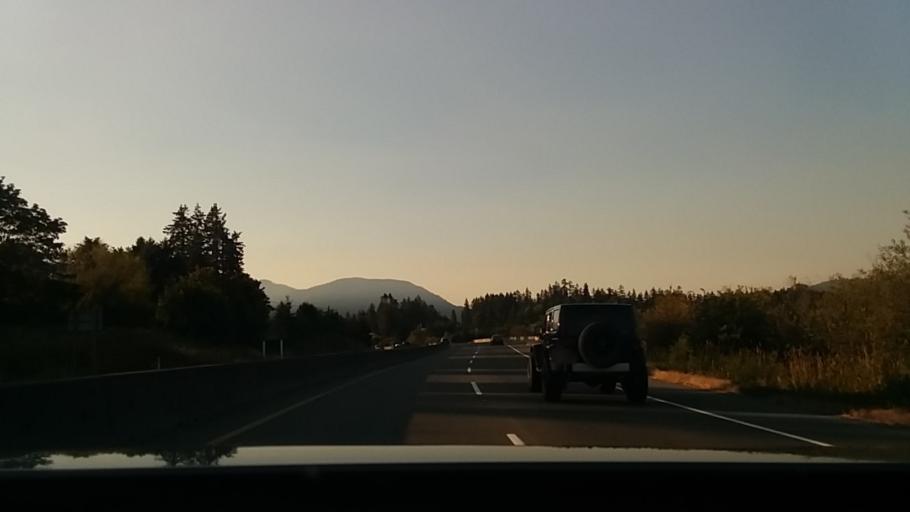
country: CA
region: British Columbia
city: Duncan
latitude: 48.7936
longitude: -123.7135
